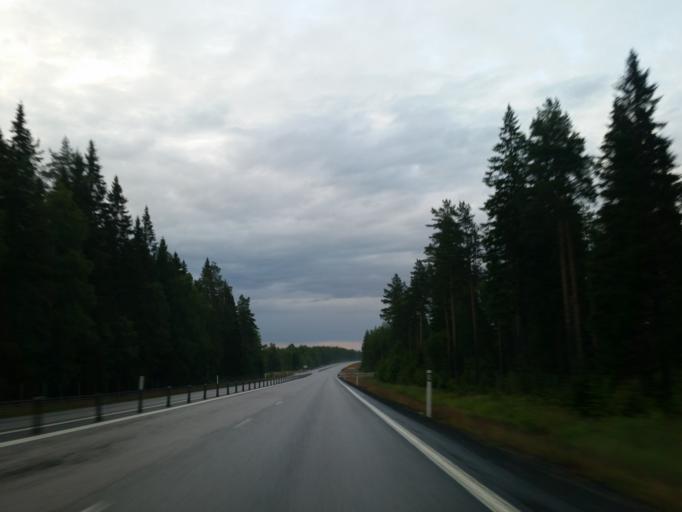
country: SE
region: Vaesterbotten
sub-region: Umea Kommun
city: Saevar
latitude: 63.9800
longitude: 20.7258
